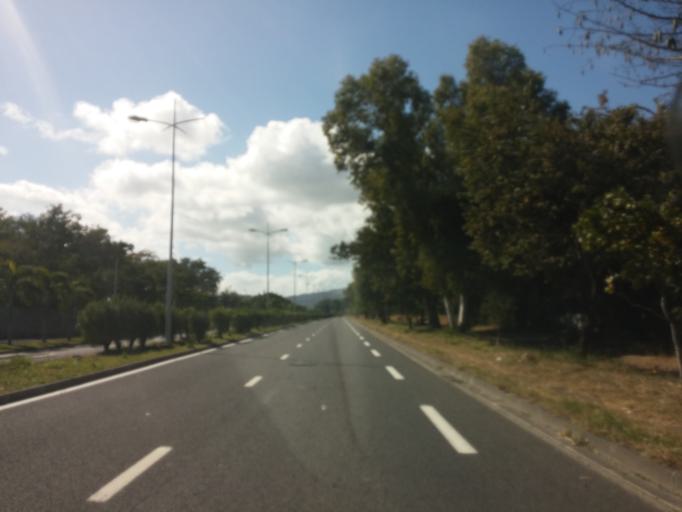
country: RE
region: Reunion
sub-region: Reunion
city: Le Port
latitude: -20.9519
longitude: 55.2968
